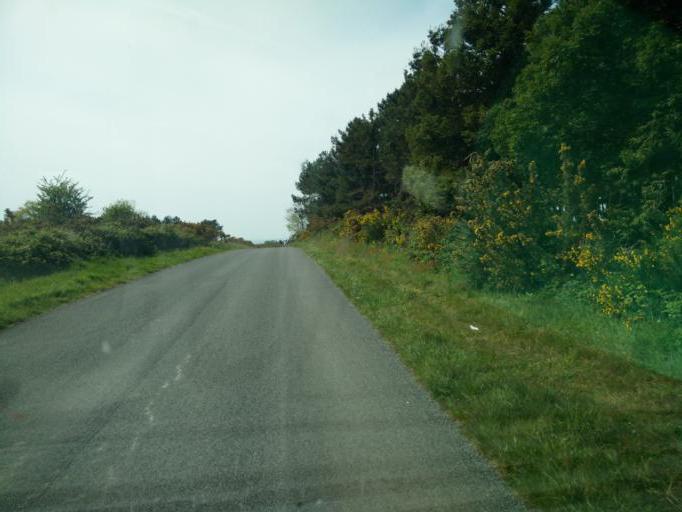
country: FR
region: Brittany
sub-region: Departement des Cotes-d'Armor
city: Saint-Cast-le-Guildo
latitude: 48.6669
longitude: -2.3053
